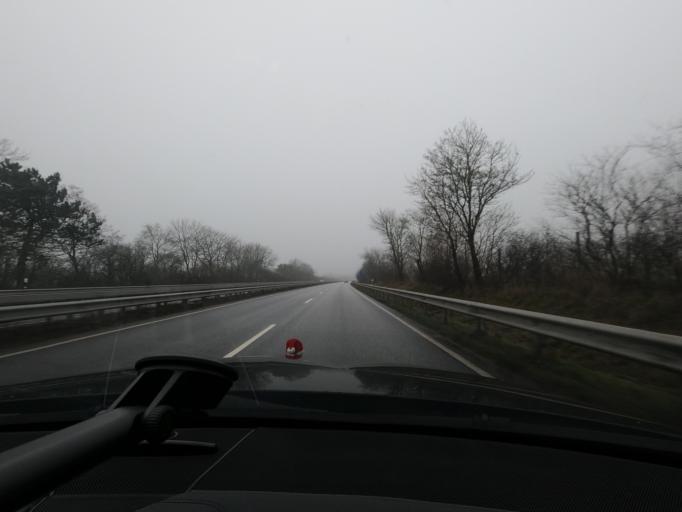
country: DE
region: Schleswig-Holstein
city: Jarplund-Weding
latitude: 54.7495
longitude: 9.4252
